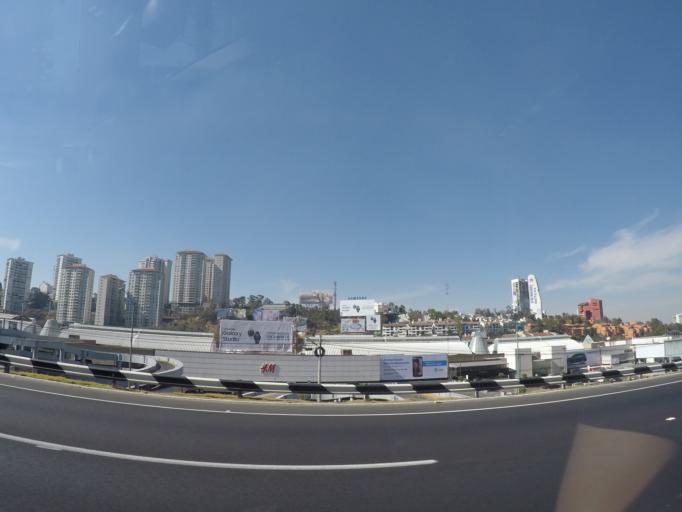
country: MX
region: Mexico City
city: Col. Bosques de las Lomas
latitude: 19.3606
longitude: -99.2715
